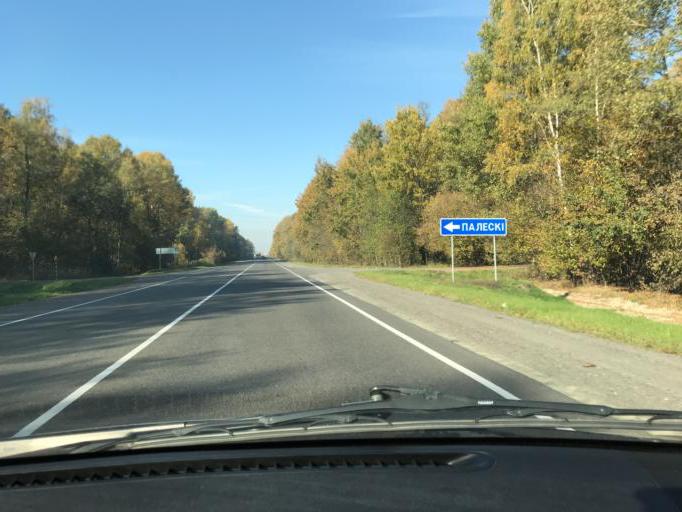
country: BY
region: Brest
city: Horad Luninyets
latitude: 52.3073
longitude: 26.6872
